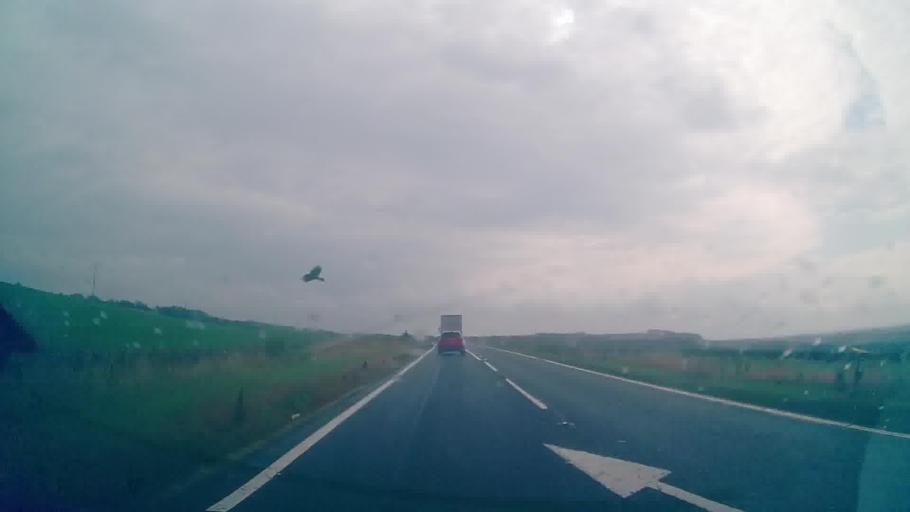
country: GB
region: Scotland
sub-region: Dumfries and Galloway
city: Lochmaben
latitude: 55.0477
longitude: -3.4564
